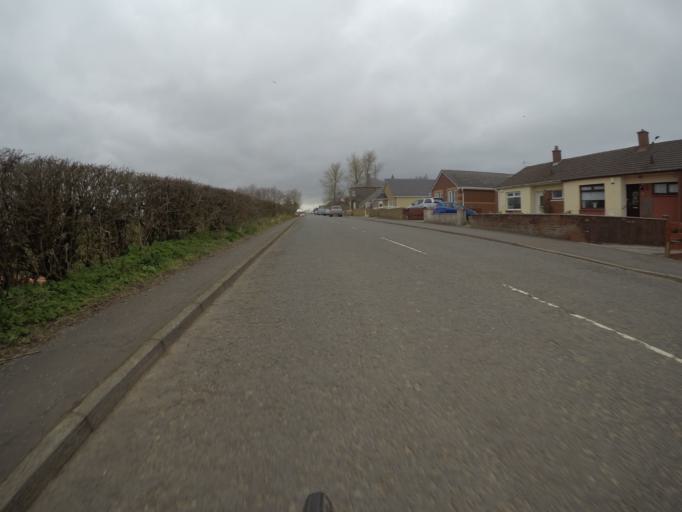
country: GB
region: Scotland
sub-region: North Ayrshire
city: Springside
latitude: 55.6172
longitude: -4.5903
